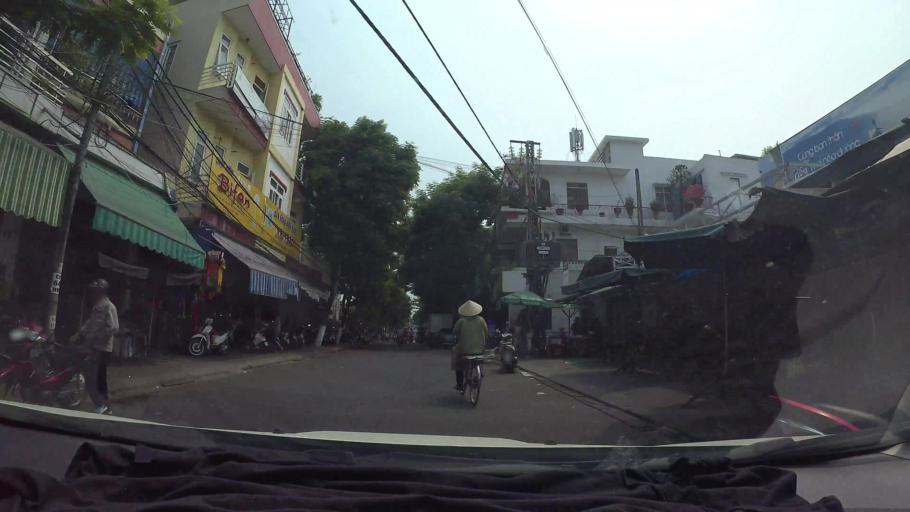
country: VN
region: Da Nang
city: Da Nang
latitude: 16.0503
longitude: 108.2182
